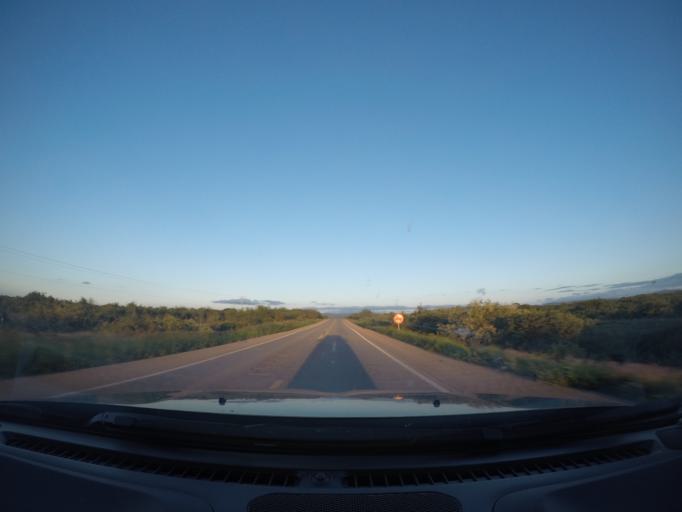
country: BR
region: Bahia
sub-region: Seabra
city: Seabra
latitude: -12.4046
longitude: -41.9544
